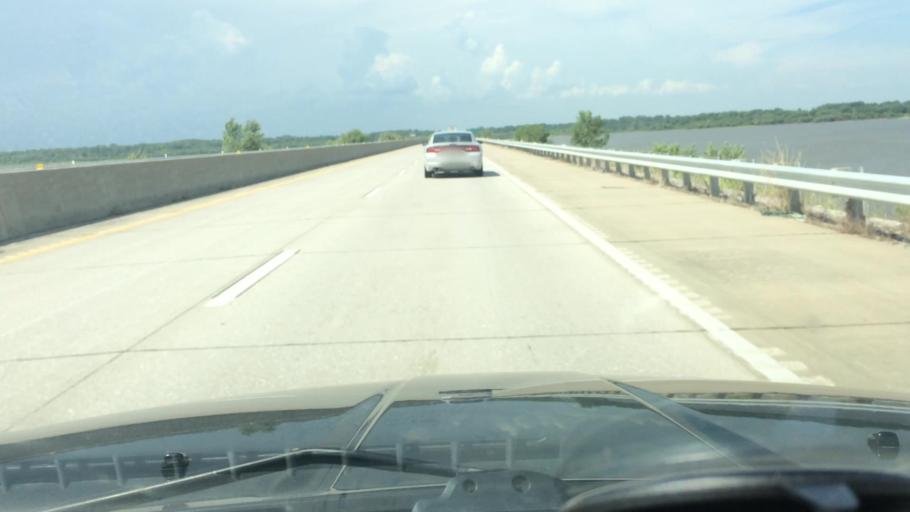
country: US
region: Missouri
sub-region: Henry County
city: Clinton
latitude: 38.2726
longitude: -93.7599
